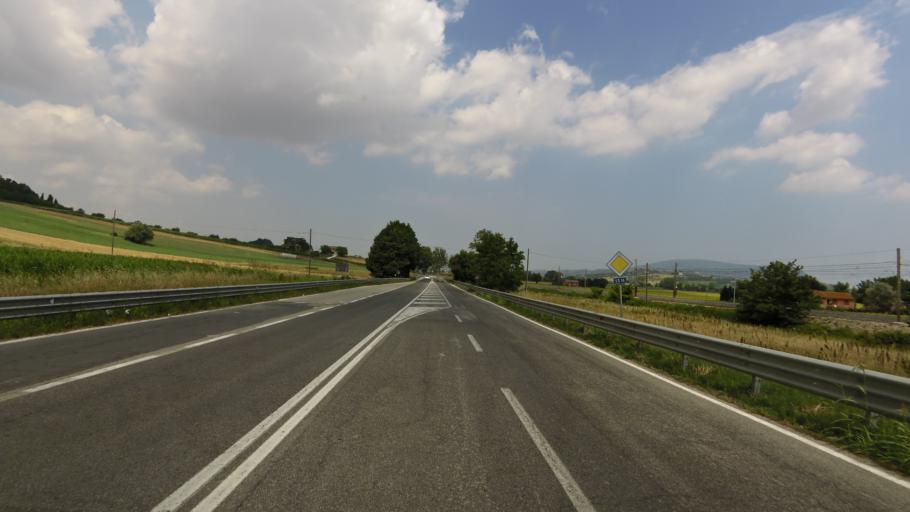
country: IT
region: The Marches
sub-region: Provincia di Ancona
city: Villa Musone
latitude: 43.4664
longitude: 13.6020
